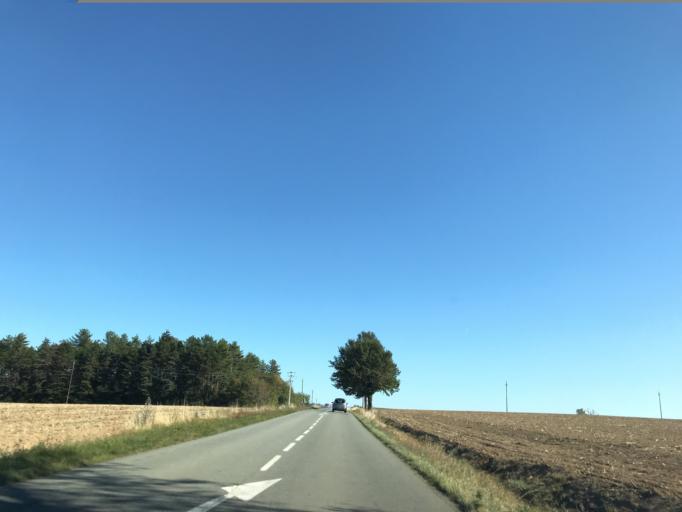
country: FR
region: Auvergne
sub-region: Departement du Puy-de-Dome
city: Courpiere
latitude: 45.7739
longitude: 3.5039
